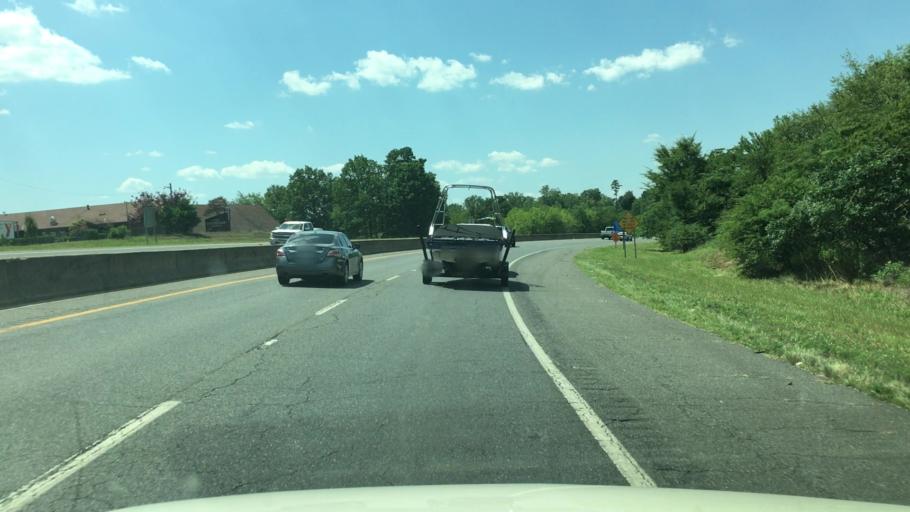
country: US
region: Arkansas
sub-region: Garland County
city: Lake Hamilton
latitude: 34.4661
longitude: -93.0858
